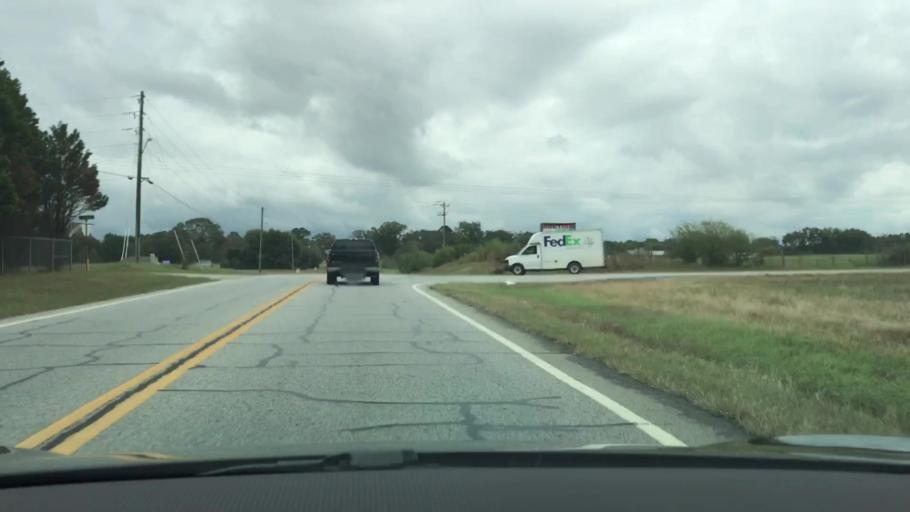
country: US
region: Georgia
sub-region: Oconee County
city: Watkinsville
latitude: 33.8412
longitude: -83.3865
